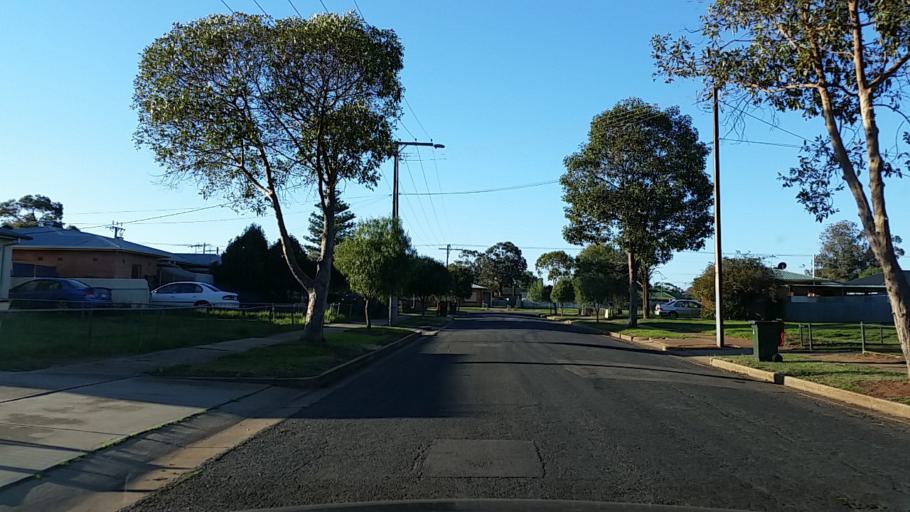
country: AU
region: South Australia
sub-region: Playford
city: Smithfield
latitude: -34.6838
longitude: 138.6669
